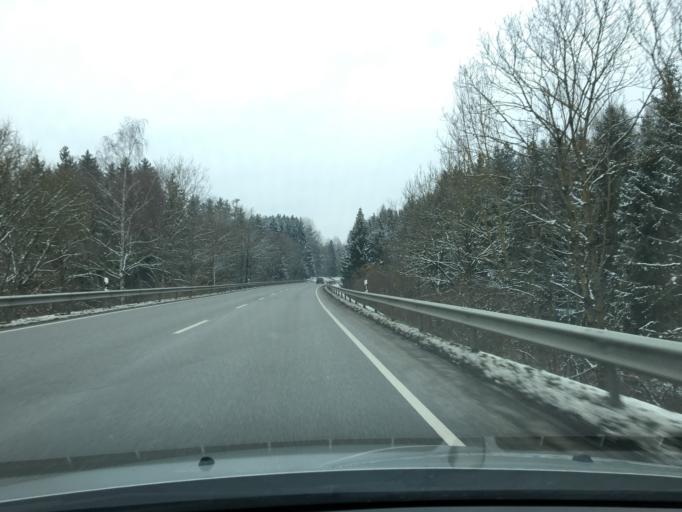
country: DE
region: Bavaria
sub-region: Lower Bavaria
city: Eging
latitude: 48.5023
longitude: 12.2136
